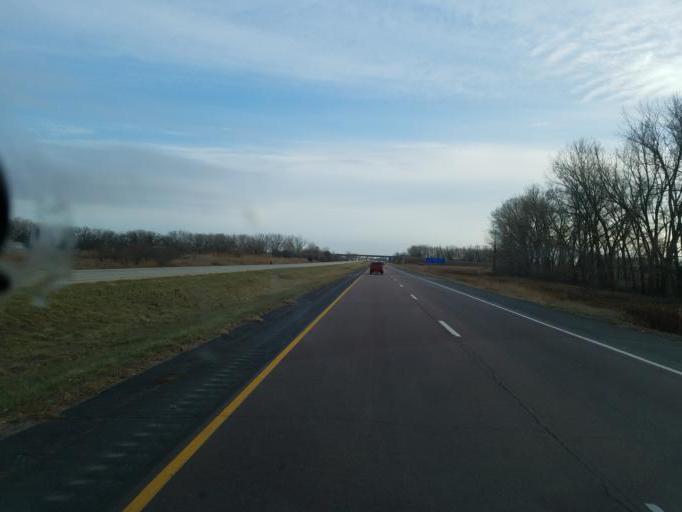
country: US
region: Iowa
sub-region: Woodbury County
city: Sergeant Bluff
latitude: 42.3861
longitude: -96.3614
